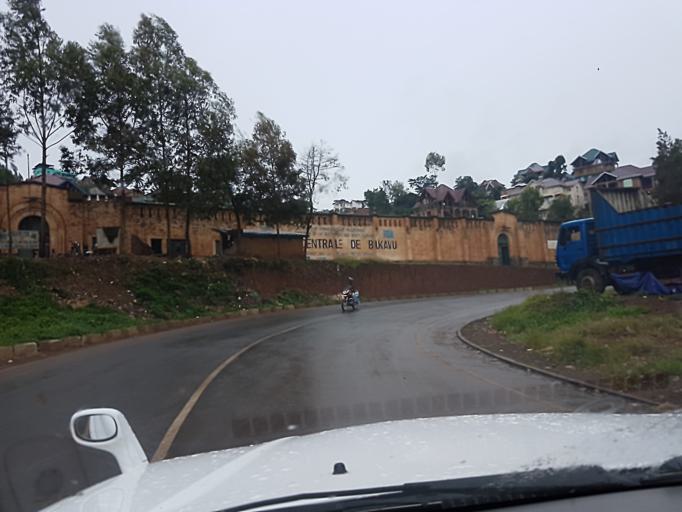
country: CD
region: South Kivu
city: Bukavu
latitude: -2.5027
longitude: 28.8526
